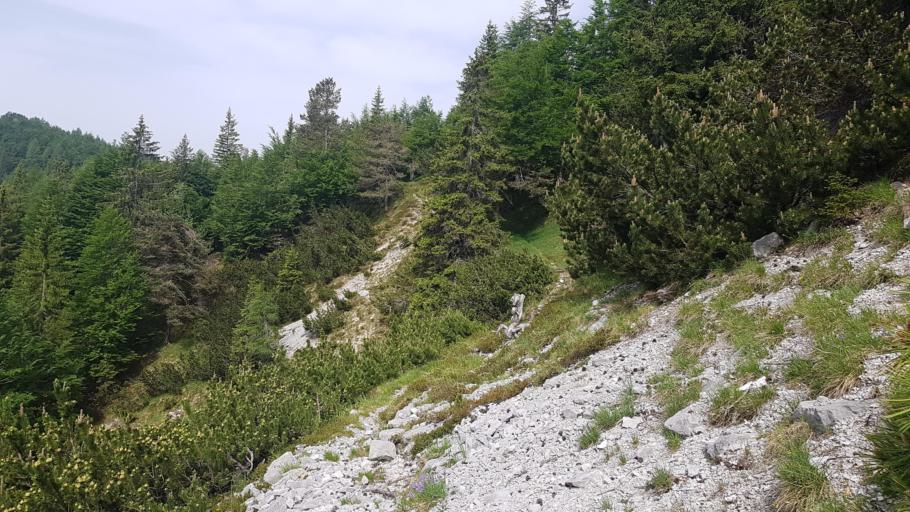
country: IT
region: Friuli Venezia Giulia
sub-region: Provincia di Udine
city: Pontebba
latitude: 46.5359
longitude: 13.2850
